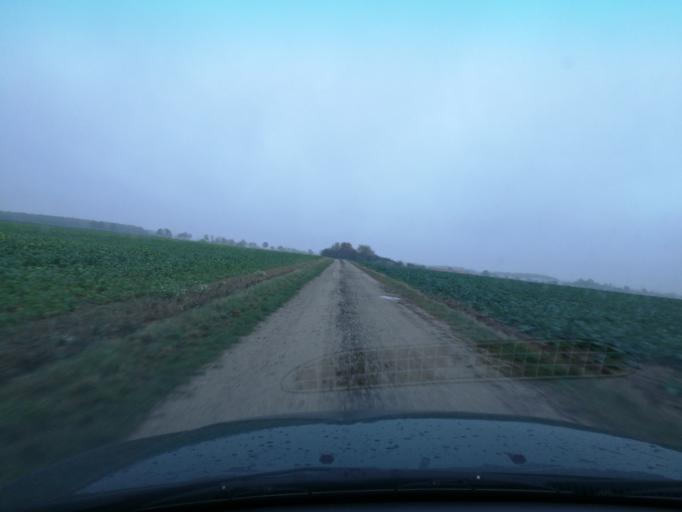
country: DE
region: Bavaria
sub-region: Regierungsbezirk Mittelfranken
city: Obermichelbach
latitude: 49.5408
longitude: 10.9076
